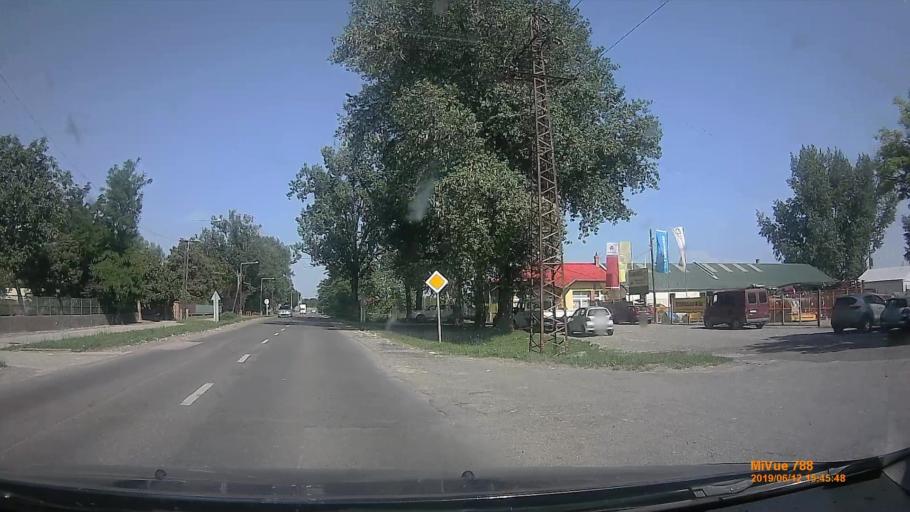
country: HU
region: Csongrad
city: Mako
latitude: 46.2169
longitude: 20.5140
